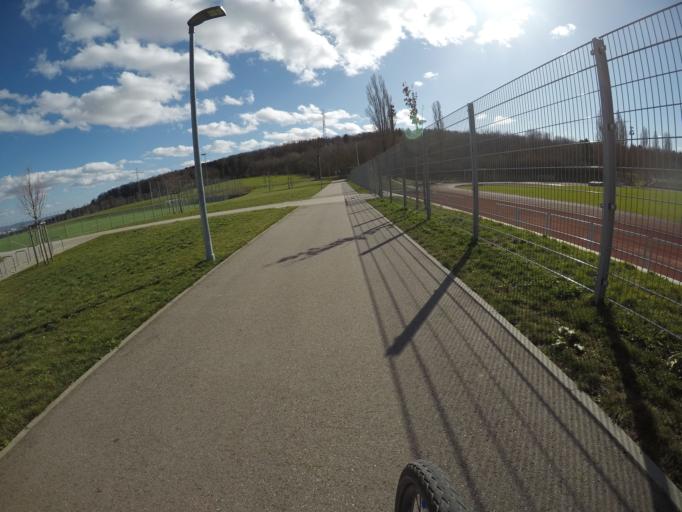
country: DE
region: Baden-Wuerttemberg
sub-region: Regierungsbezirk Stuttgart
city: Leinfelden-Echterdingen
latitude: 48.6881
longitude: 9.1426
